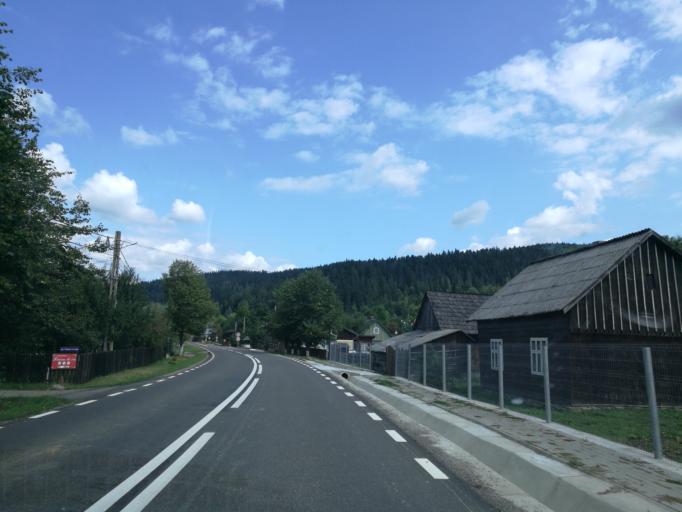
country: RO
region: Suceava
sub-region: Comuna Sucevita
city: Sucevita
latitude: 47.7633
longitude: 25.6922
